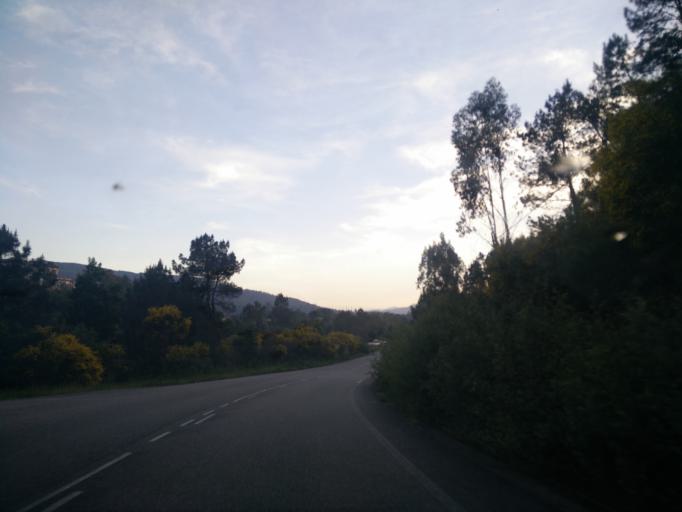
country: ES
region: Galicia
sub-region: Provincia de Pontevedra
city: Mondariz
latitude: 42.2388
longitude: -8.4542
